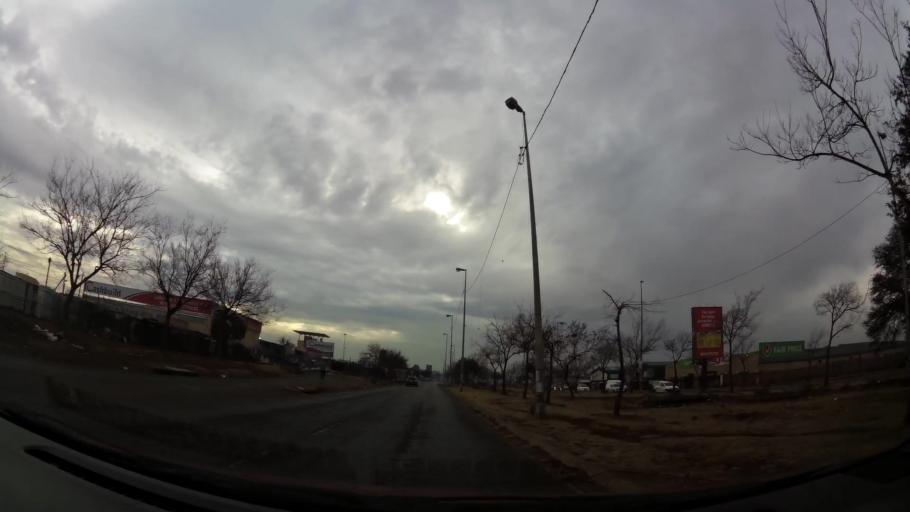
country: ZA
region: Gauteng
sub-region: City of Johannesburg Metropolitan Municipality
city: Soweto
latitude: -26.2884
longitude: 27.8473
